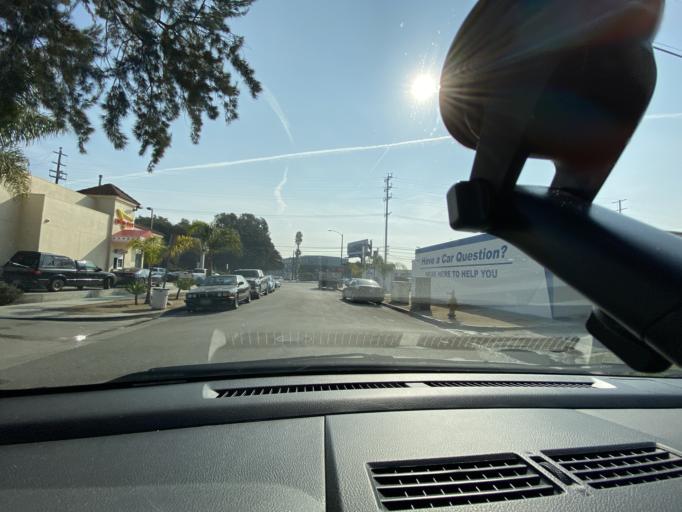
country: US
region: California
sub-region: Los Angeles County
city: Culver City
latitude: 34.0265
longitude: -118.3947
